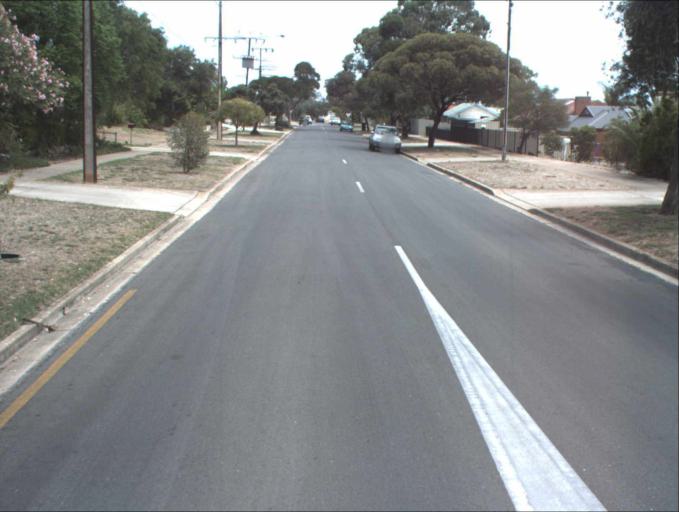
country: AU
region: South Australia
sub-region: Port Adelaide Enfield
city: Enfield
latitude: -34.8488
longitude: 138.6107
